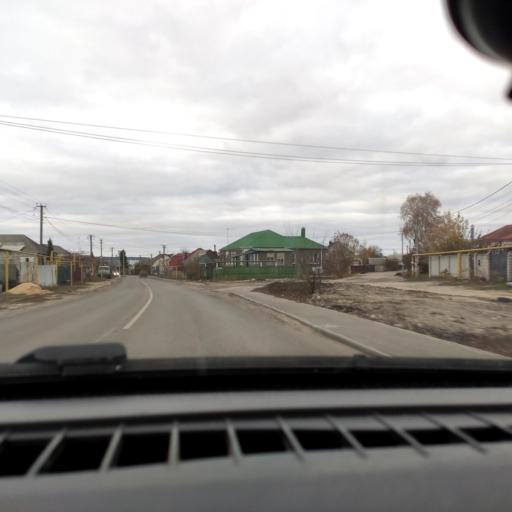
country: RU
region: Voronezj
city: Podgornoye
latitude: 51.7255
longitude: 39.1438
